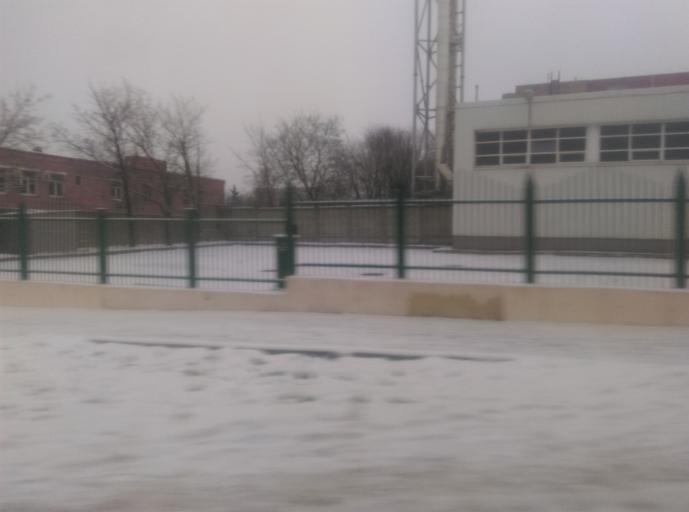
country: RU
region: Moscow
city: Mikhalkovo
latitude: 55.6936
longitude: 37.4264
